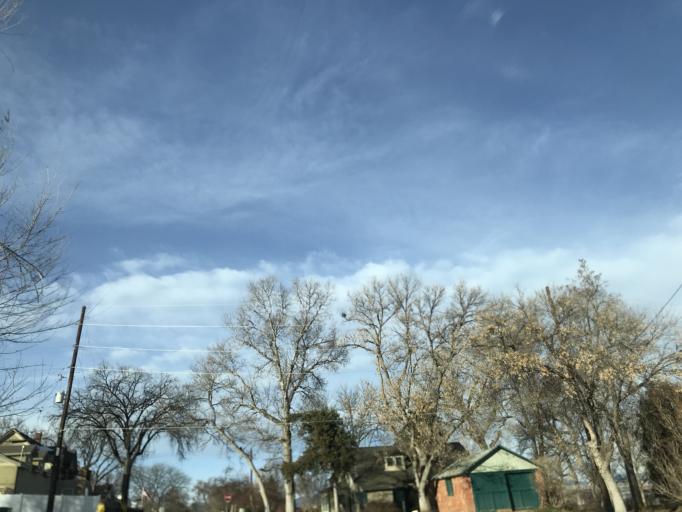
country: US
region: Colorado
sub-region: Arapahoe County
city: Littleton
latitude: 39.6096
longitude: -105.0117
